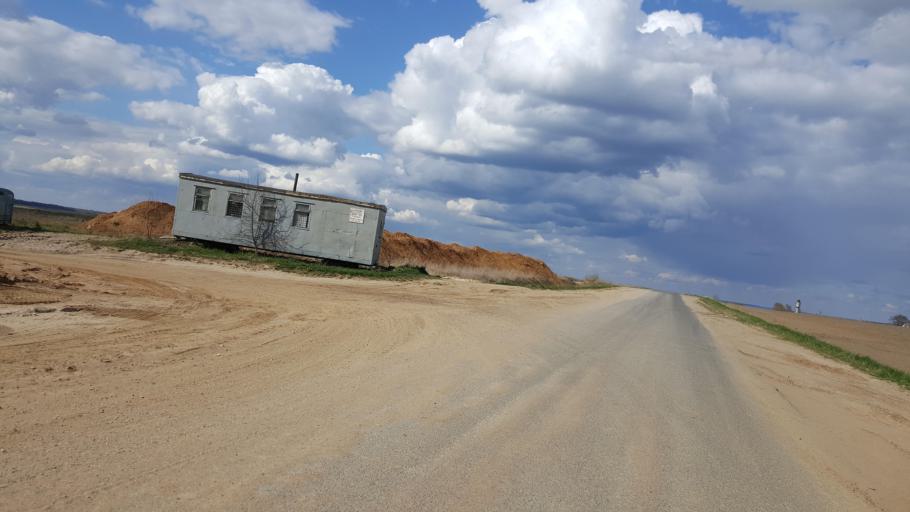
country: BY
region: Brest
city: Kamyanyets
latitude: 52.4381
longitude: 23.6515
